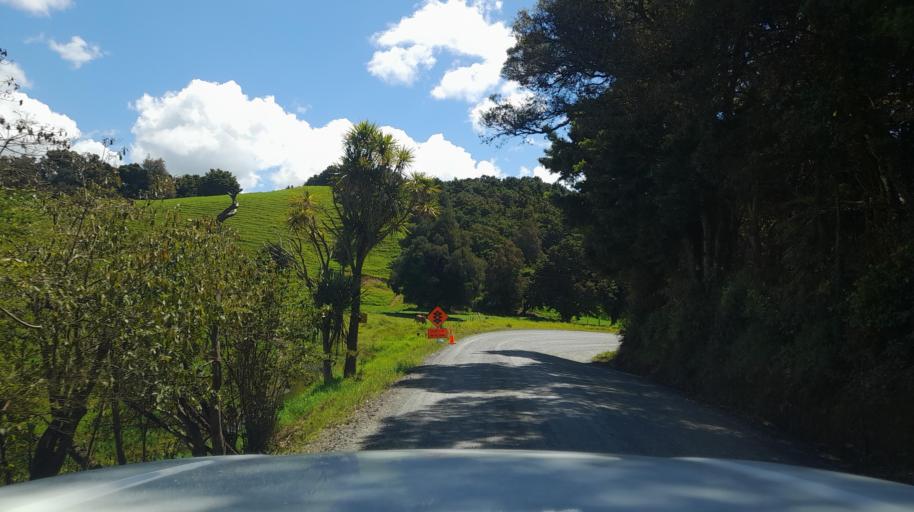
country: NZ
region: Northland
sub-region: Far North District
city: Kaitaia
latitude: -35.1117
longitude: 173.3960
